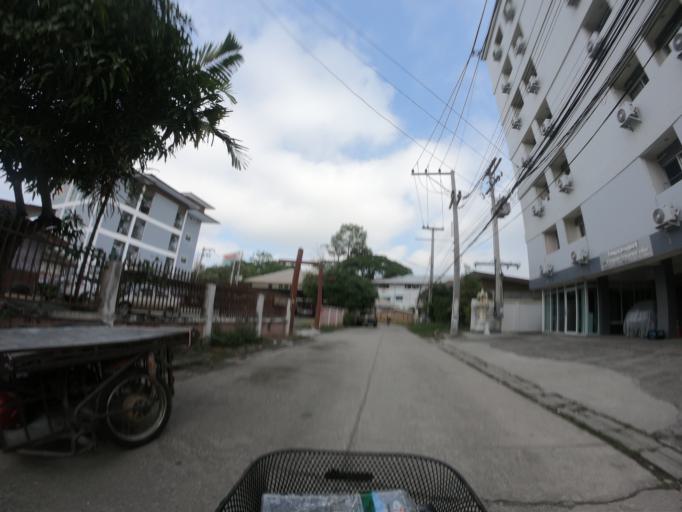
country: TH
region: Chiang Mai
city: Chiang Mai
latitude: 18.7575
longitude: 98.9716
